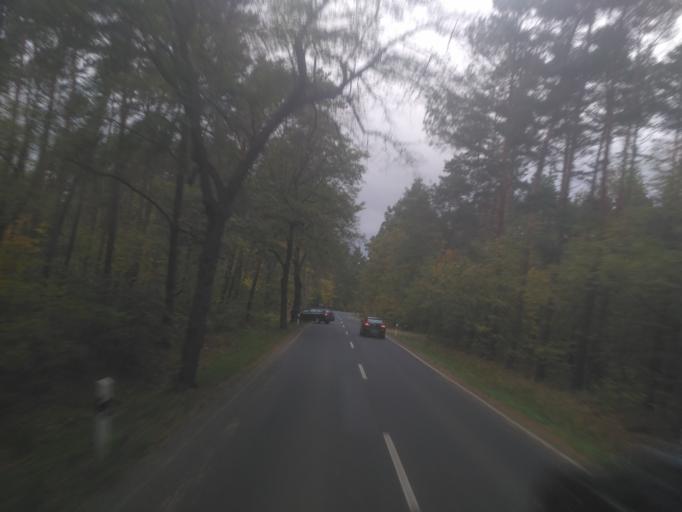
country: DE
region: Brandenburg
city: Merzdorf
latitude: 51.3972
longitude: 13.5042
